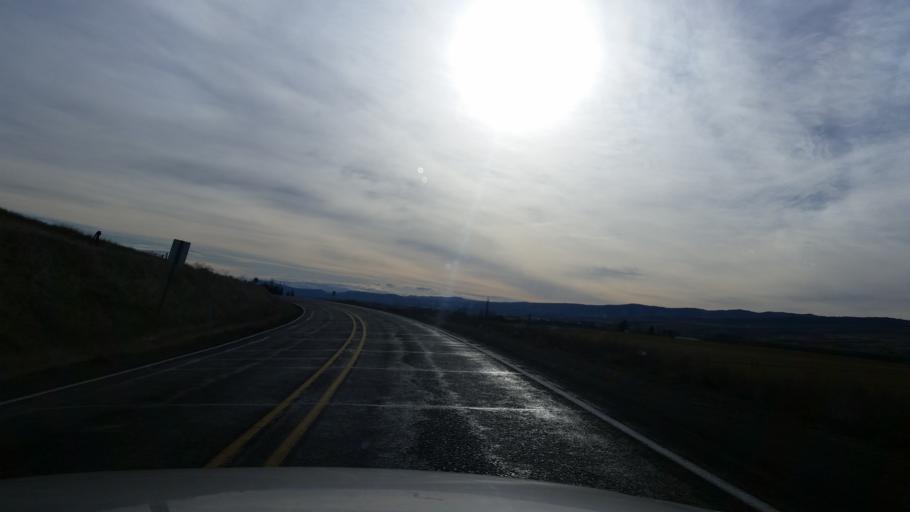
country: US
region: Washington
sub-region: Kittitas County
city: Ellensburg
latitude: 47.1097
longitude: -120.7154
